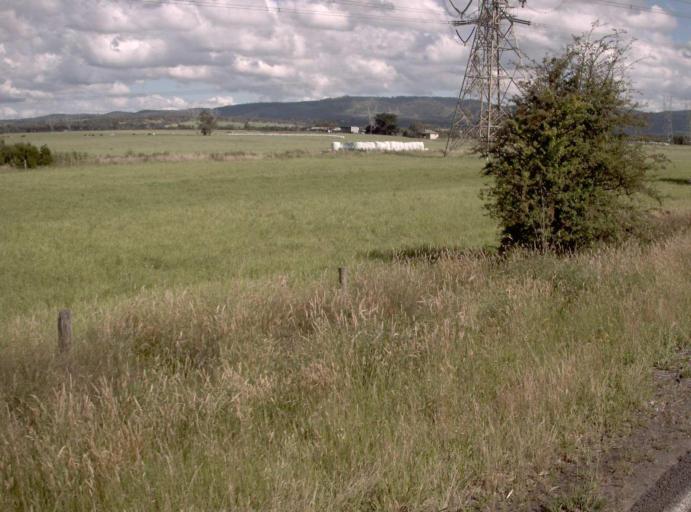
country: AU
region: Victoria
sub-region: Latrobe
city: Morwell
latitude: -38.2775
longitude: 146.4322
